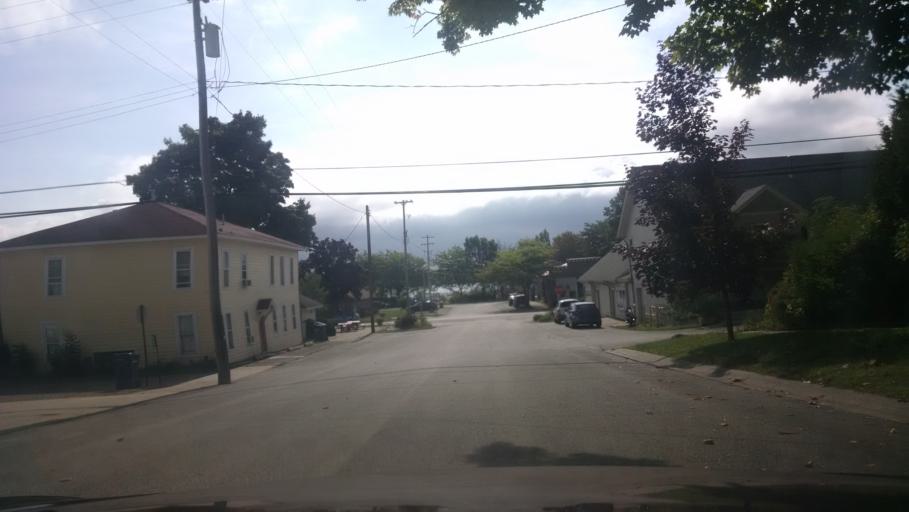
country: US
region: Michigan
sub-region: Leelanau County
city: Leland
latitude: 44.9782
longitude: -85.6510
